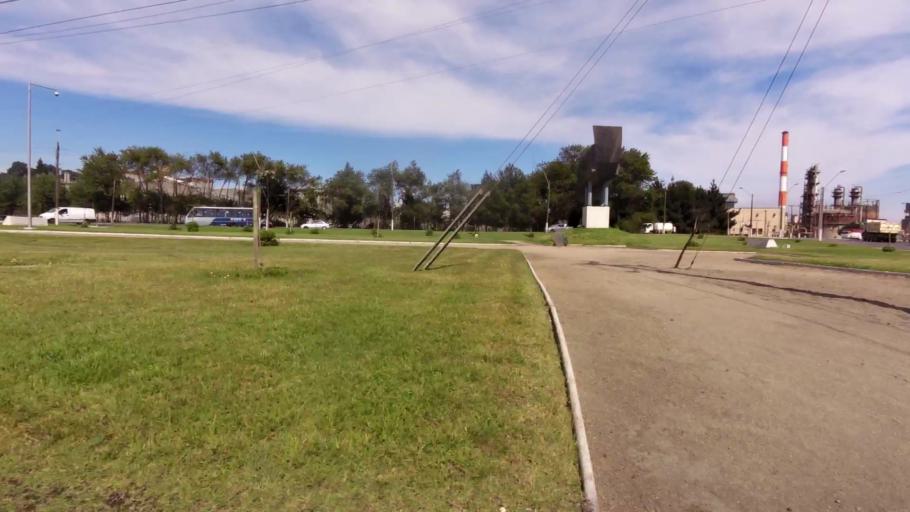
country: CL
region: Biobio
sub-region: Provincia de Concepcion
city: Talcahuano
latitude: -36.7405
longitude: -73.1189
